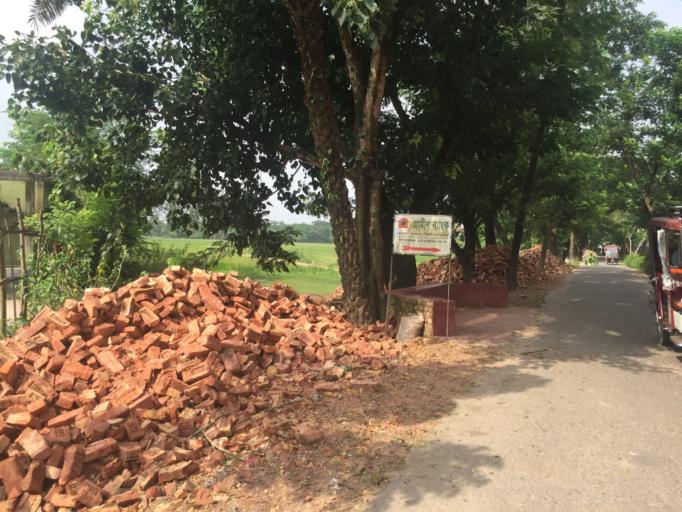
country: BD
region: Barisal
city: Mathba
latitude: 22.2157
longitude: 89.9158
